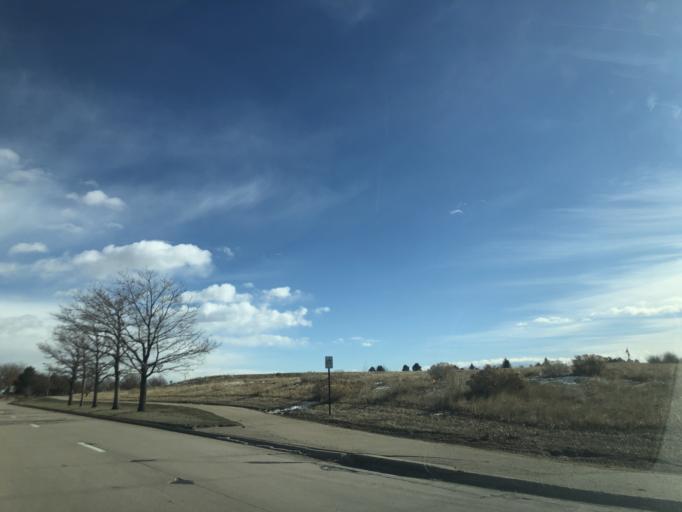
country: US
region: Colorado
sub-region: Douglas County
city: Meridian
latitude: 39.5487
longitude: -104.8583
